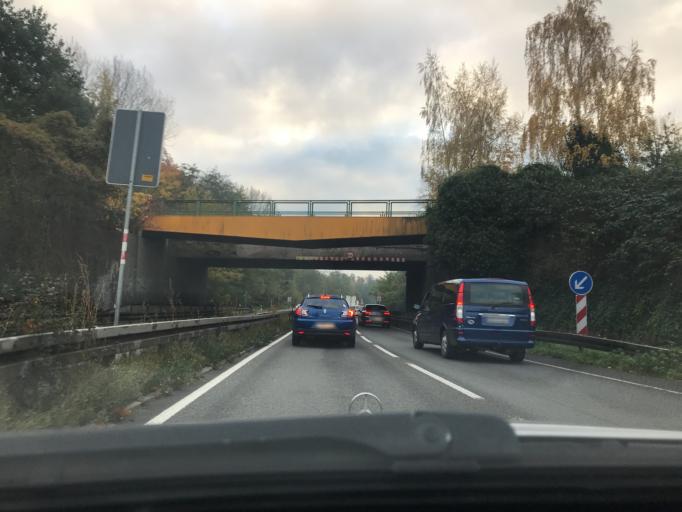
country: DE
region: North Rhine-Westphalia
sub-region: Regierungsbezirk Munster
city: Gladbeck
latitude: 51.5334
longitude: 6.9868
